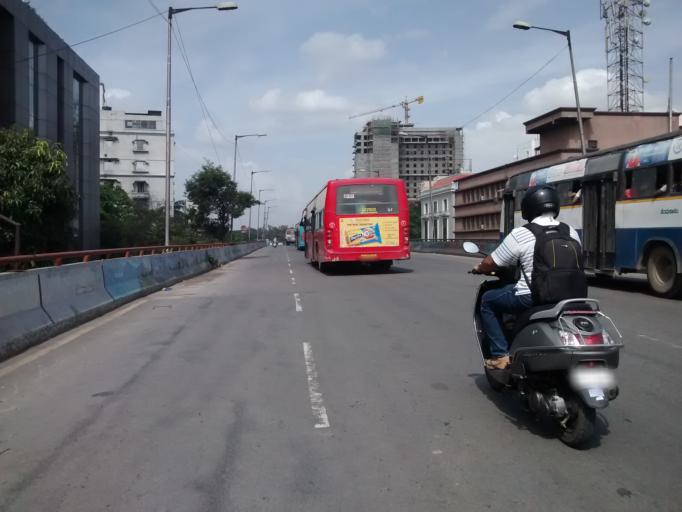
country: IN
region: Karnataka
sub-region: Bangalore Urban
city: Bangalore
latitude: 12.9807
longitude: 77.5756
